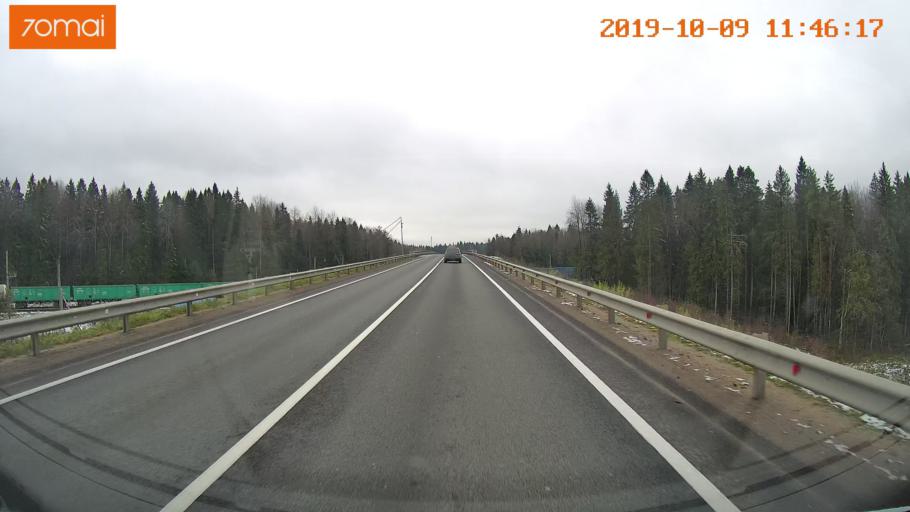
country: RU
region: Vologda
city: Gryazovets
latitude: 58.8555
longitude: 40.2010
